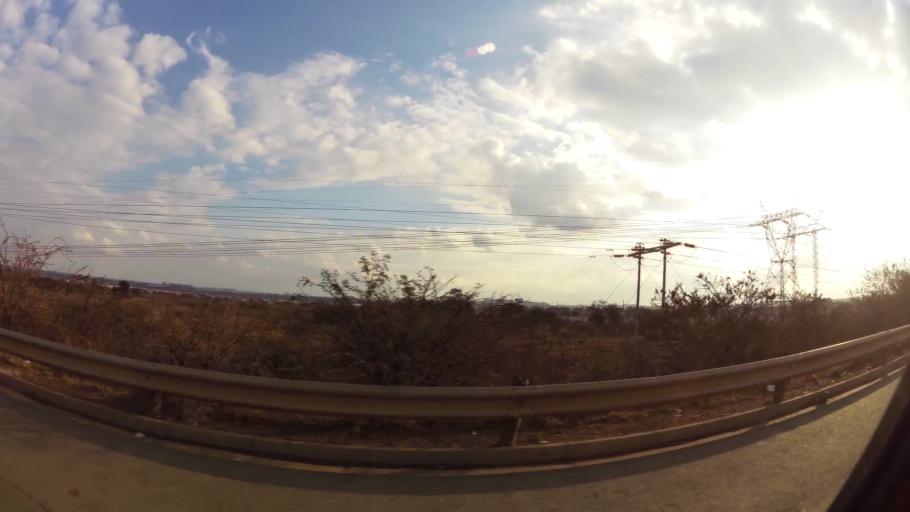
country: ZA
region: Gauteng
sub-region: Sedibeng District Municipality
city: Vereeniging
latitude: -26.6386
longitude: 27.8717
